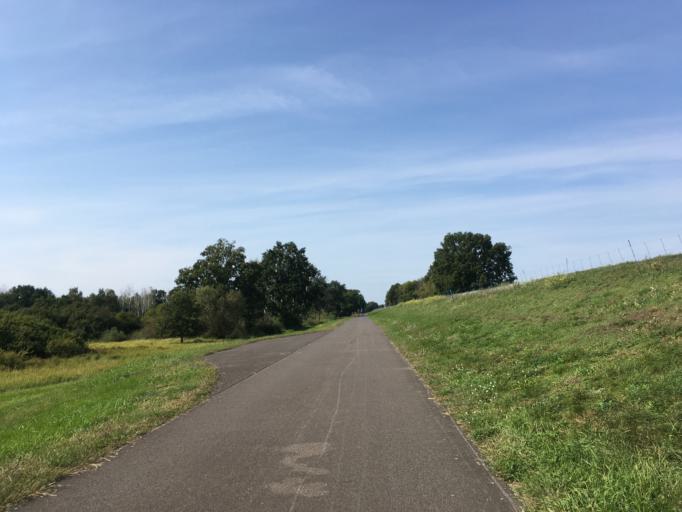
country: DE
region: Brandenburg
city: Vogelsang
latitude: 52.1769
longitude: 14.6977
